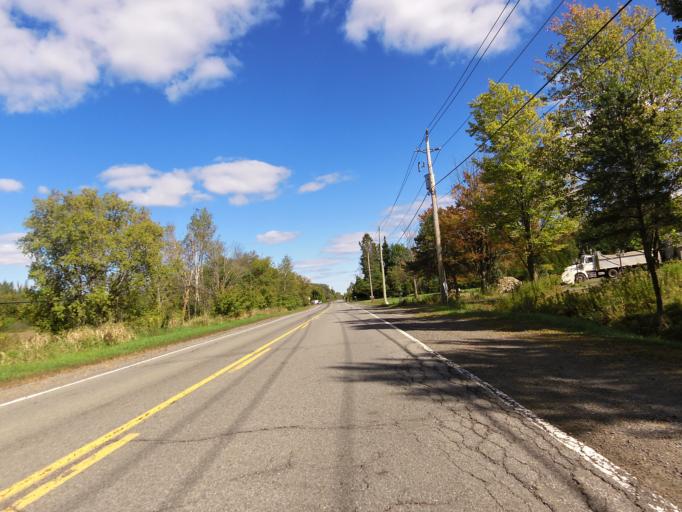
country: CA
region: Ontario
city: Ottawa
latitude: 45.3489
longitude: -75.5079
